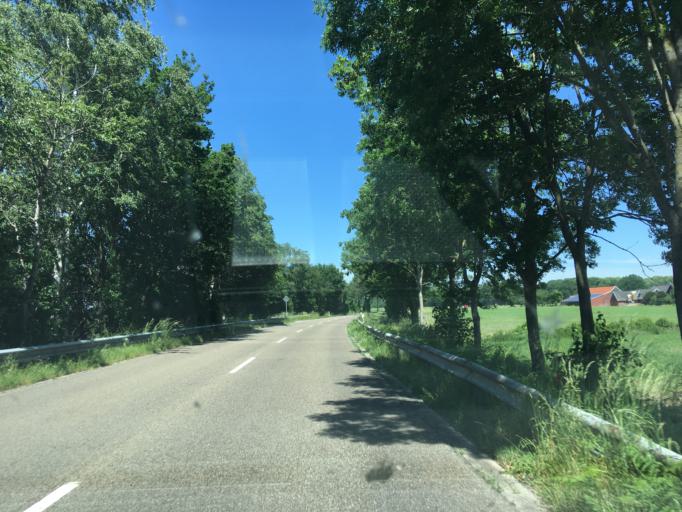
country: DE
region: North Rhine-Westphalia
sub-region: Regierungsbezirk Munster
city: Raesfeld
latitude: 51.7903
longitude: 6.8139
